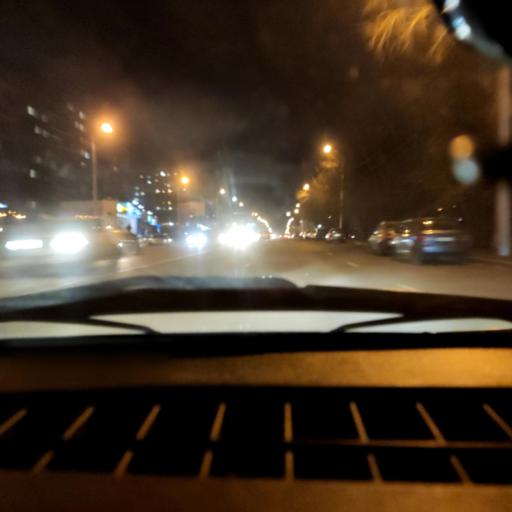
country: RU
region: Bashkortostan
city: Ufa
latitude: 54.7016
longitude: 55.9962
